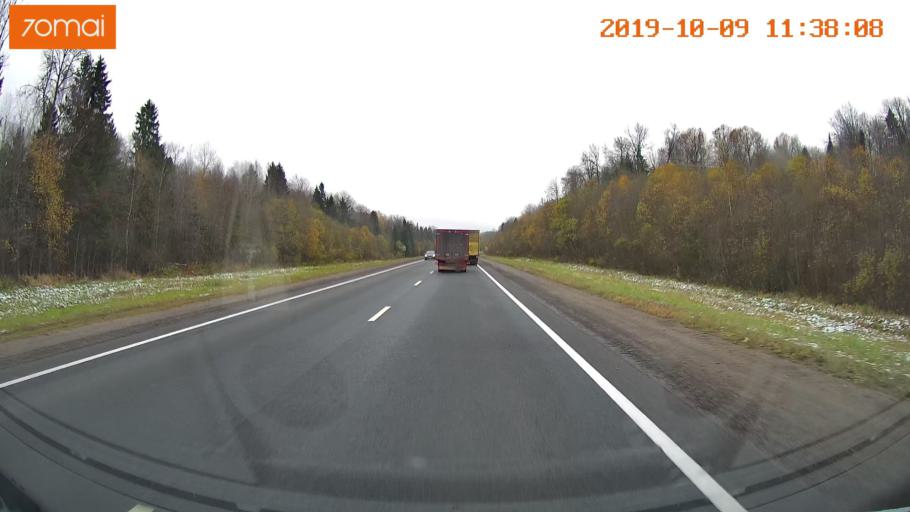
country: RU
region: Vologda
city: Gryazovets
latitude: 58.9714
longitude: 40.1530
